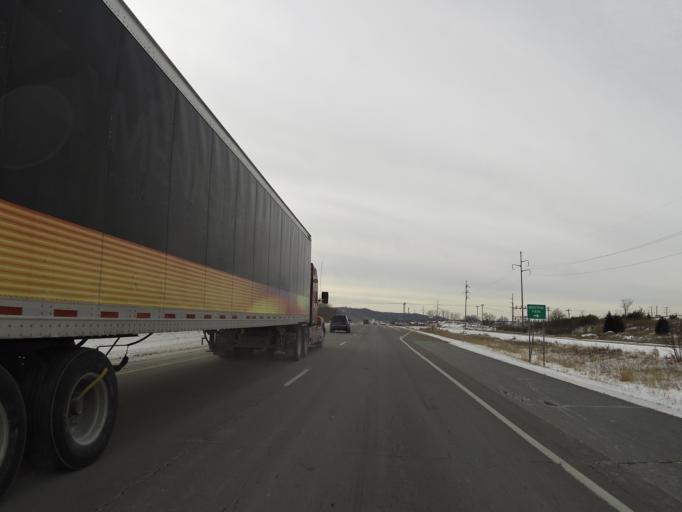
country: US
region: Minnesota
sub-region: Carver County
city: Carver
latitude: 44.7159
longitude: -93.5878
